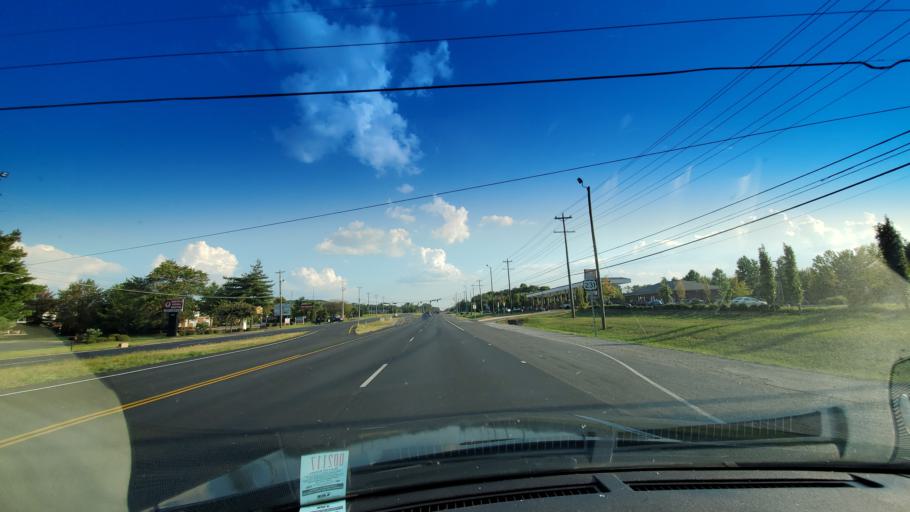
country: US
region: Tennessee
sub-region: Rutherford County
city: Murfreesboro
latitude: 35.7835
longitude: -86.4011
